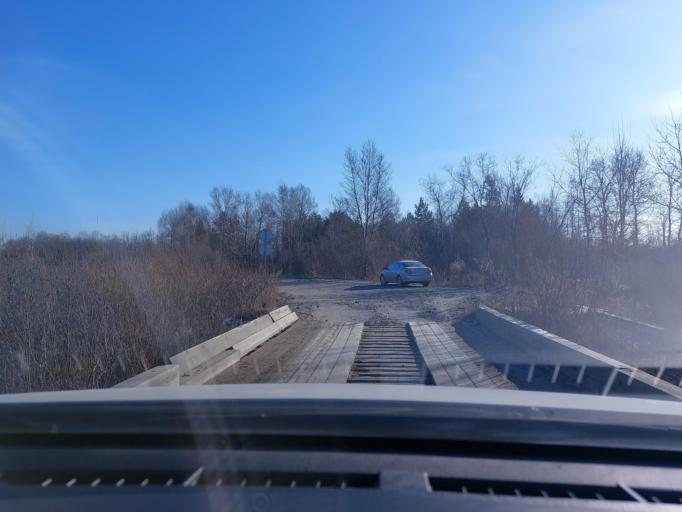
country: RU
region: Irkutsk
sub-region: Irkutskiy Rayon
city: Irkutsk
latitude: 52.3003
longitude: 104.2769
